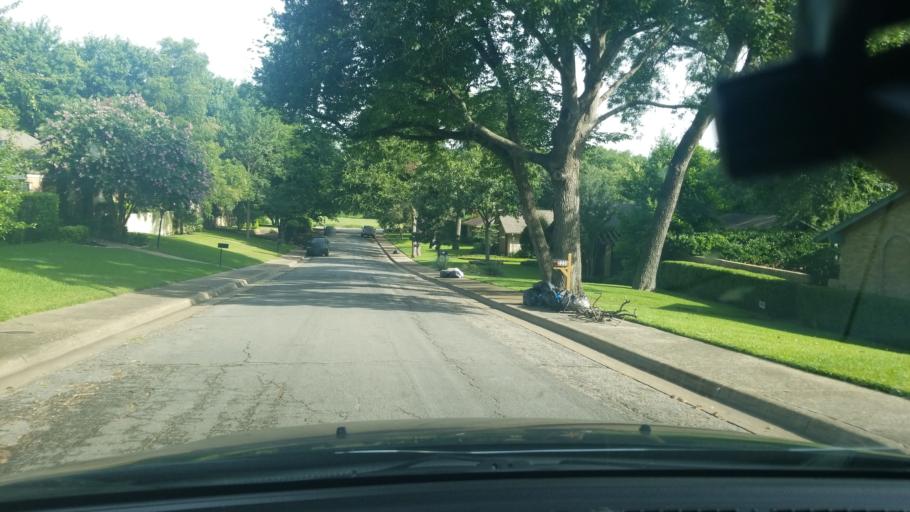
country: US
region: Texas
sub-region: Dallas County
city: Highland Park
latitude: 32.8071
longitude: -96.7091
